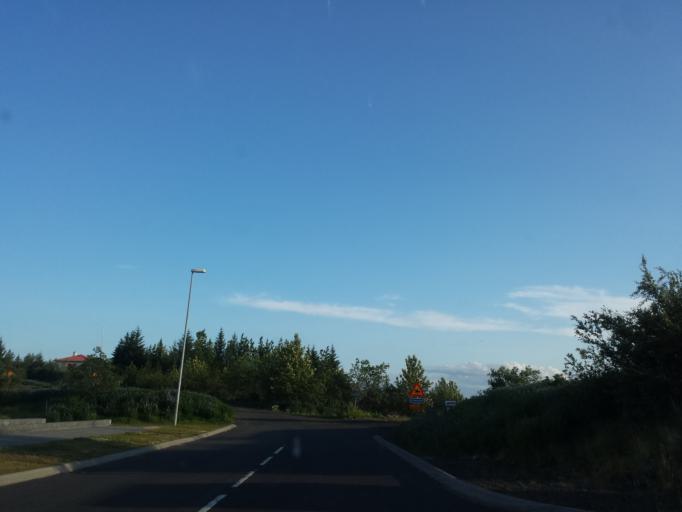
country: IS
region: Capital Region
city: Mosfellsbaer
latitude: 64.0957
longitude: -21.7784
